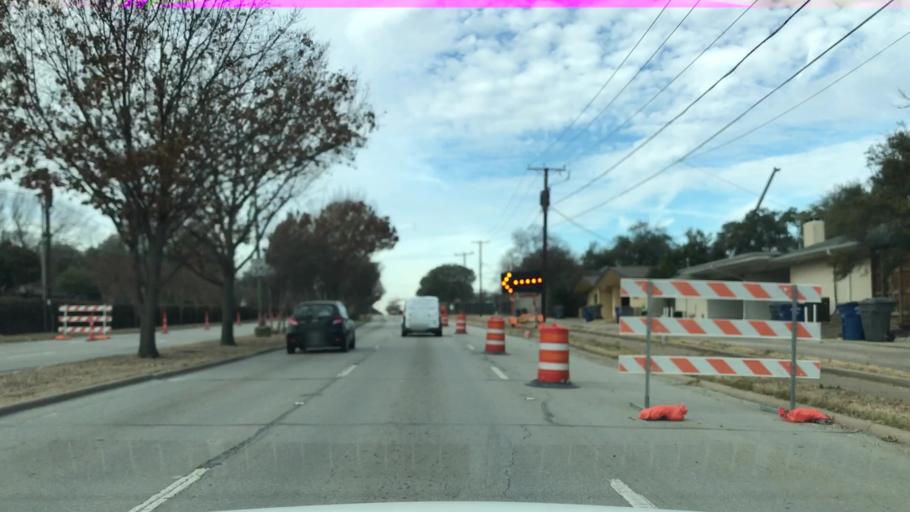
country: US
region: Texas
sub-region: Dallas County
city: University Park
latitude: 32.8801
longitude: -96.7833
